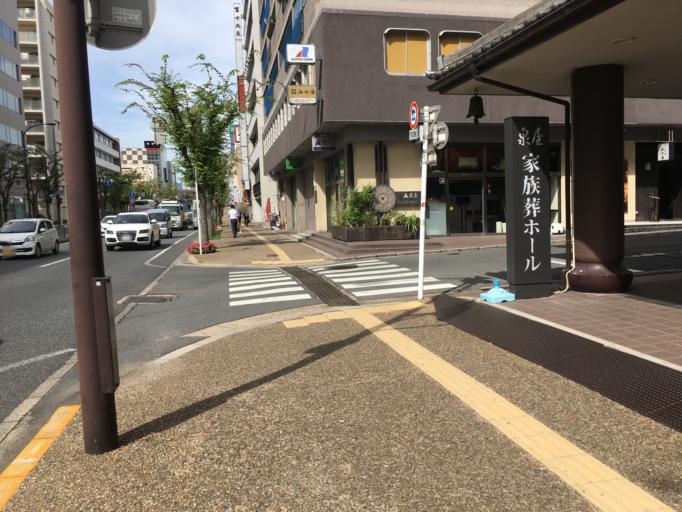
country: JP
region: Nara
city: Nara-shi
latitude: 34.6843
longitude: 135.8096
